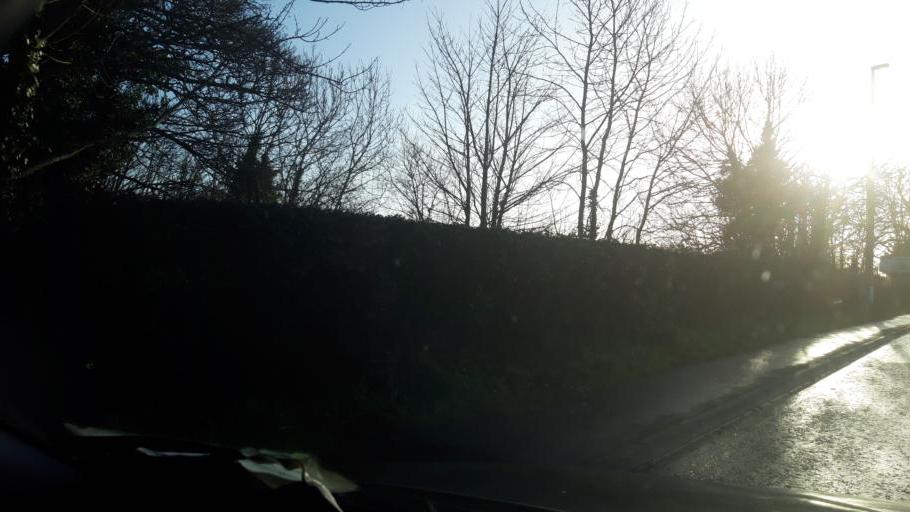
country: GB
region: Northern Ireland
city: Garvagh
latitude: 54.9910
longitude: -6.6838
